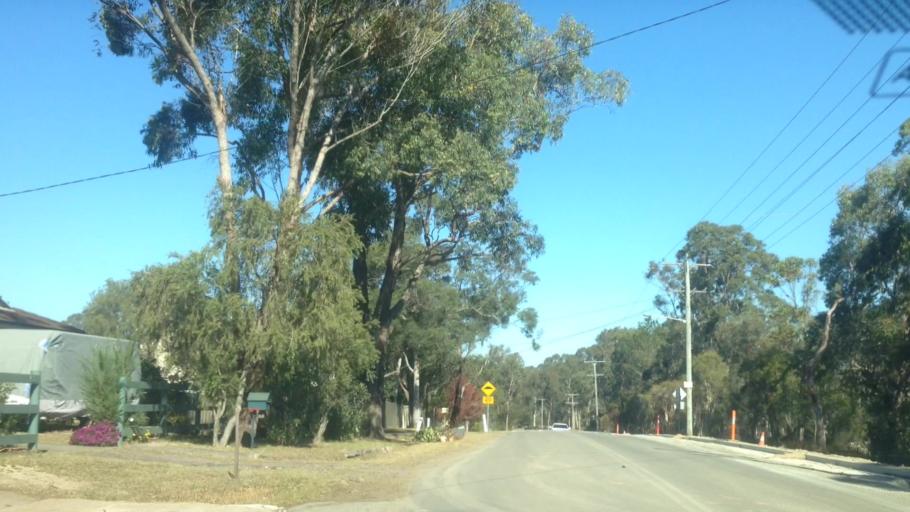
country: AU
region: New South Wales
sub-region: Lake Macquarie Shire
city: Cooranbong
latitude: -33.0930
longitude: 151.4512
